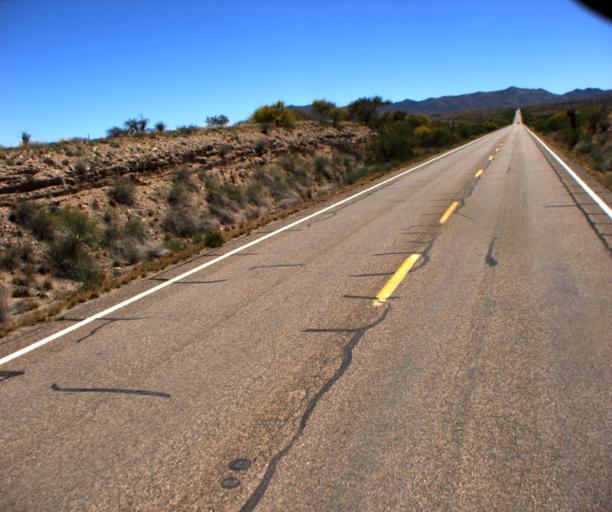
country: US
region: Arizona
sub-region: Pima County
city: Vail
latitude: 31.9891
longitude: -110.6826
